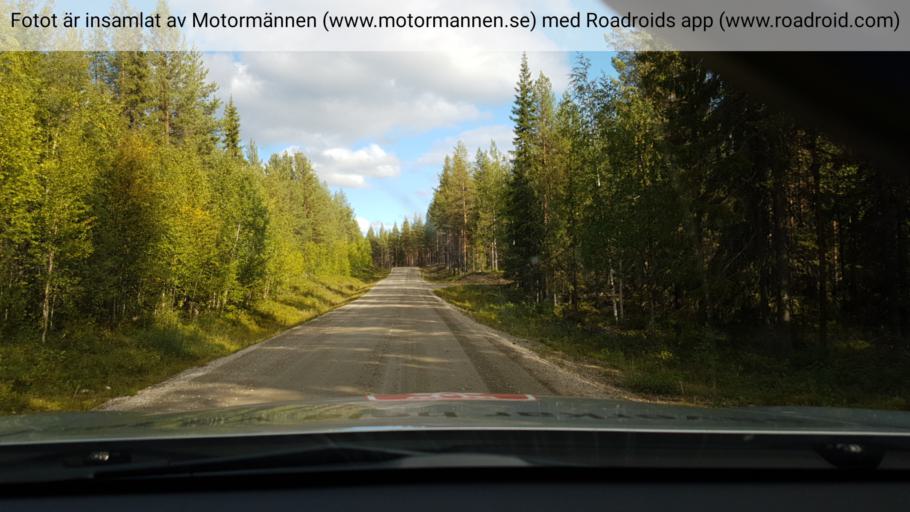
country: SE
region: Vaesterbotten
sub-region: Sorsele Kommun
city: Sorsele
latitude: 65.3616
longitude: 18.0319
